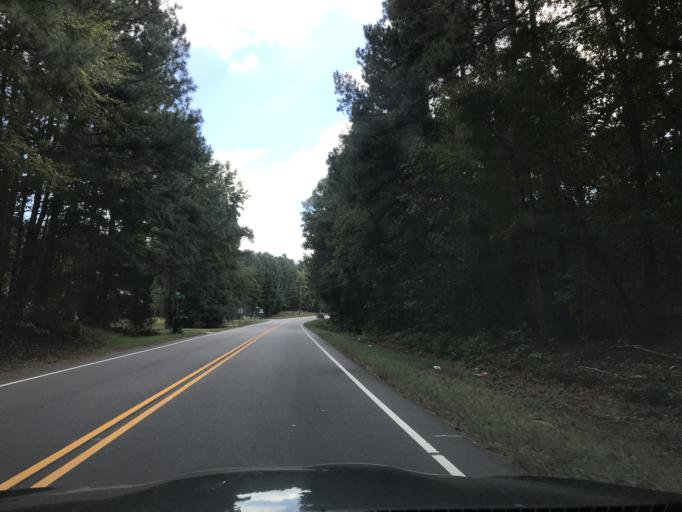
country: US
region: North Carolina
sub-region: Wake County
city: Wake Forest
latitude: 35.9254
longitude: -78.5258
